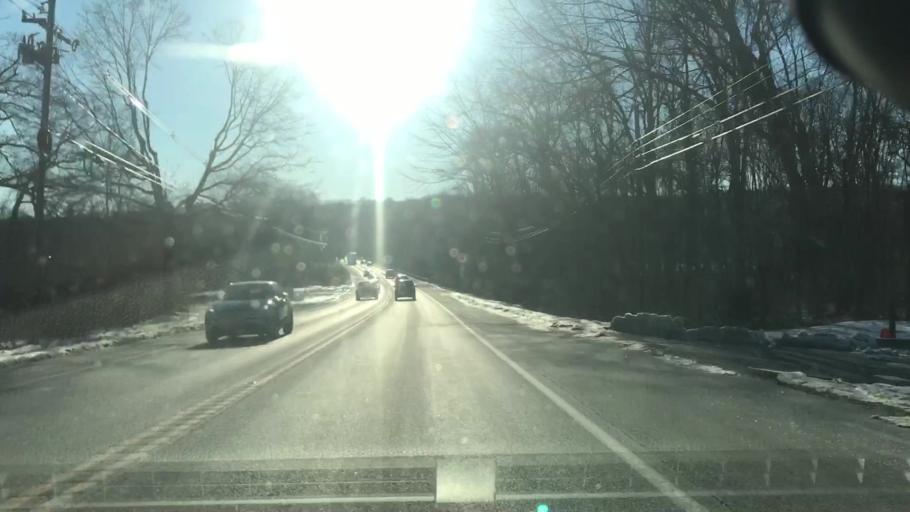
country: US
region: New Jersey
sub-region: Morris County
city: Chester
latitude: 40.8002
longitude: -74.7113
